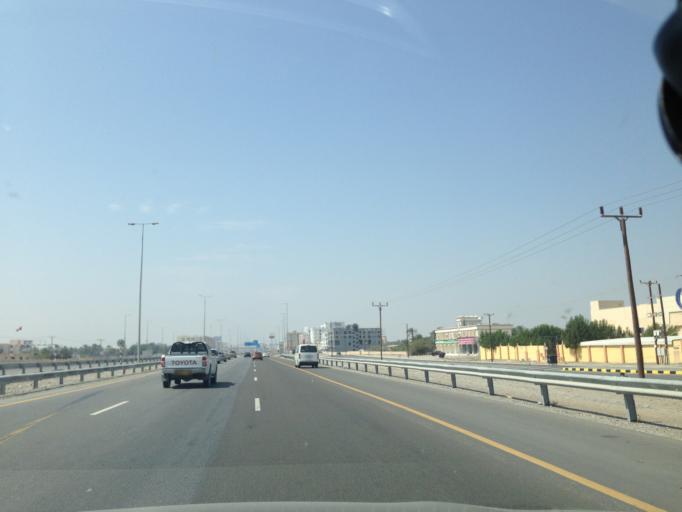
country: OM
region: Al Batinah
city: Barka'
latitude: 23.6633
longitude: 57.9036
